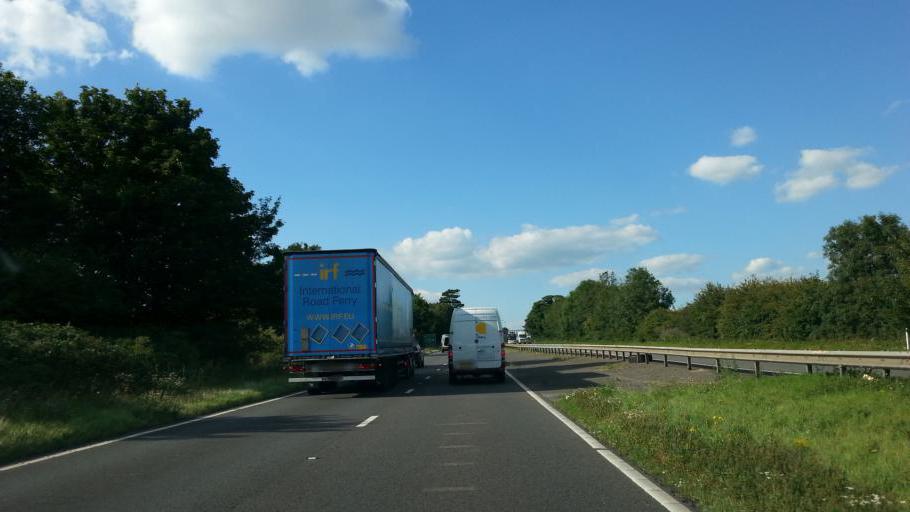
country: GB
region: England
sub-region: Lincolnshire
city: Grantham
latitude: 52.8579
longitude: -0.6289
